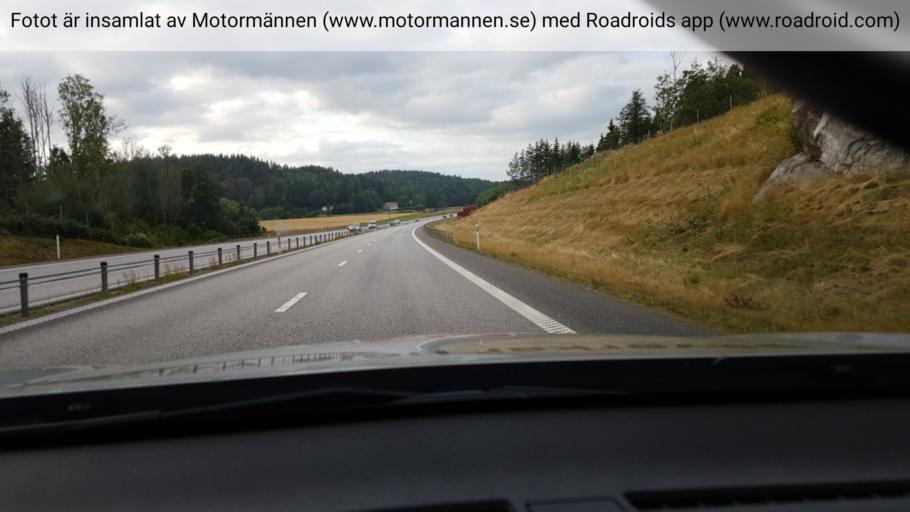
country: SE
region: Vaestra Goetaland
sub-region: Lilla Edets Kommun
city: Lodose
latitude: 58.0672
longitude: 12.1597
